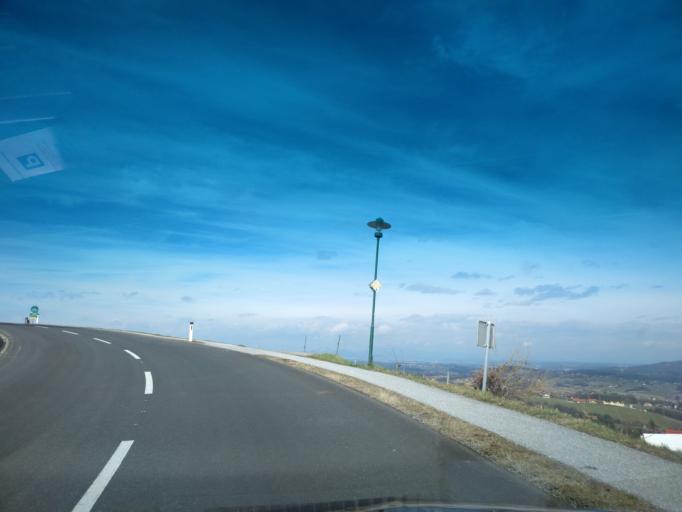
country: AT
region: Styria
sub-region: Politischer Bezirk Leibnitz
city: Kitzeck im Sausal
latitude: 46.7902
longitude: 15.4444
